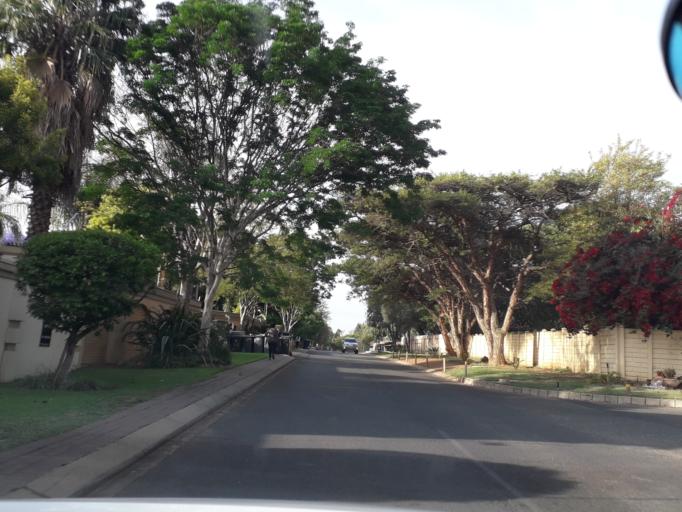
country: ZA
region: Gauteng
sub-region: City of Johannesburg Metropolitan Municipality
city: Diepsloot
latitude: -26.0318
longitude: 27.9909
